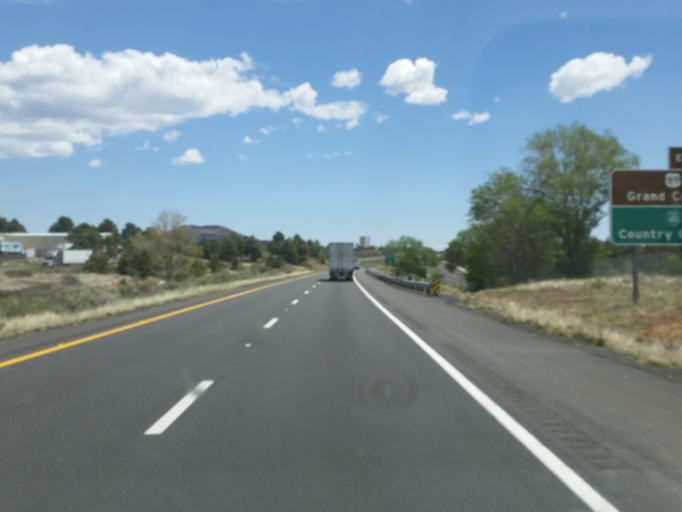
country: US
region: Arizona
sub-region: Coconino County
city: Flagstaff
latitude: 35.2114
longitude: -111.5945
